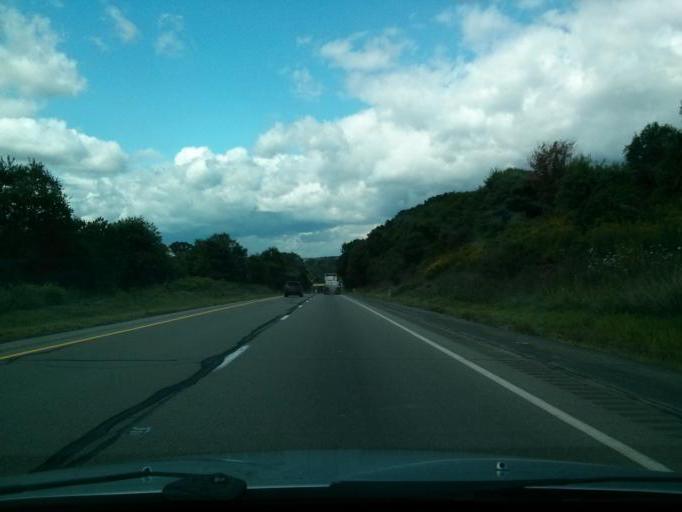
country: US
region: Pennsylvania
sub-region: Jefferson County
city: Brookville
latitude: 41.1705
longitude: -79.0601
